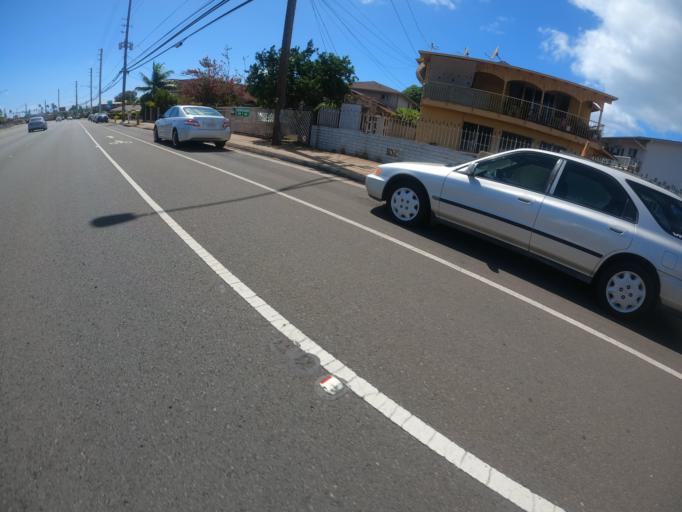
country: US
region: Hawaii
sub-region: Honolulu County
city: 'Ewa Beach
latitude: 21.3138
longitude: -158.0112
